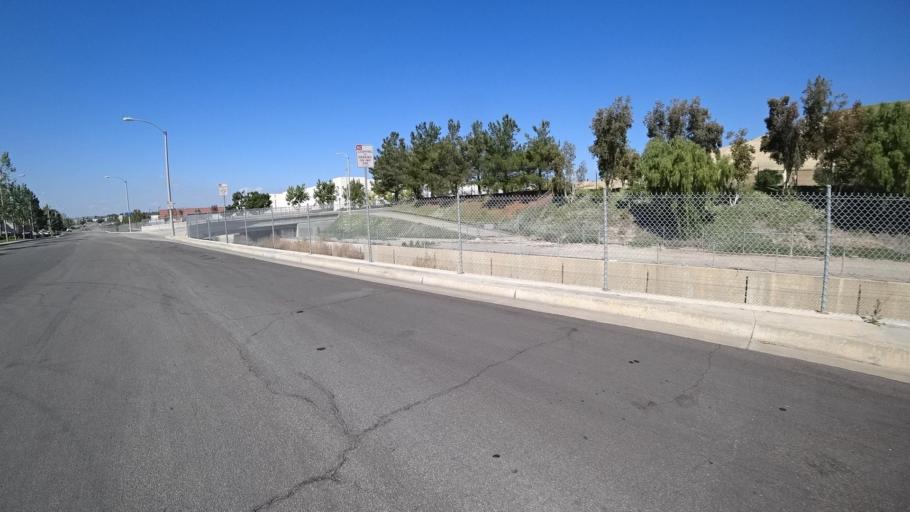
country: US
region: California
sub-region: Los Angeles County
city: Diamond Bar
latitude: 34.0294
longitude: -117.8281
